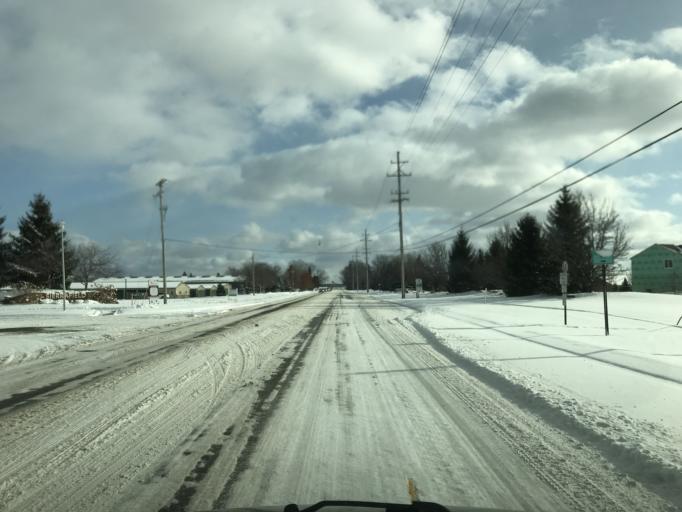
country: US
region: Michigan
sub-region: Kent County
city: Byron Center
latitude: 42.8264
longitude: -85.6975
